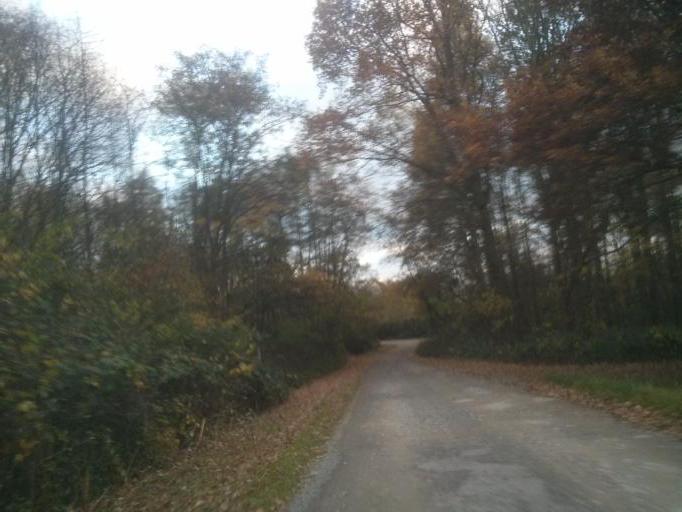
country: DE
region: North Rhine-Westphalia
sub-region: Regierungsbezirk Koln
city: Poll
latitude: 50.9065
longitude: 7.0081
